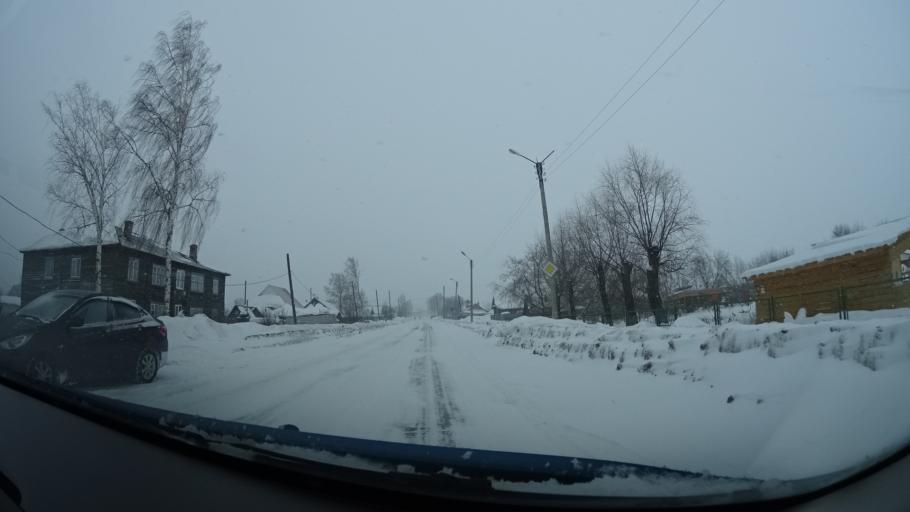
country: RU
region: Perm
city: Kuyeda
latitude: 56.4308
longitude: 55.5767
